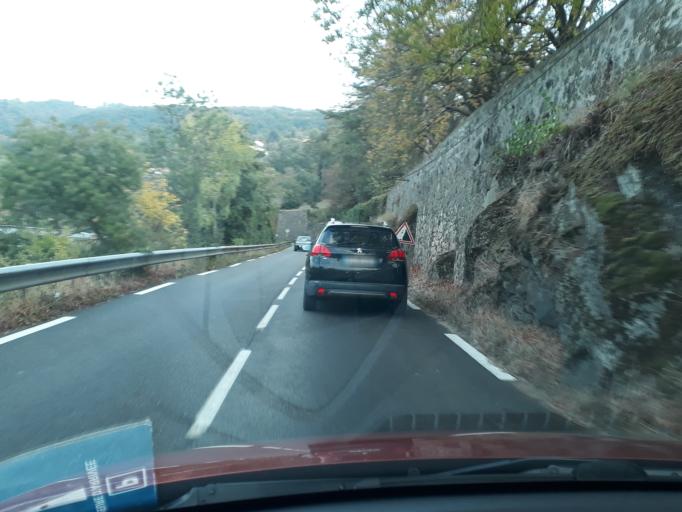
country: FR
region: Rhone-Alpes
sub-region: Departement de l'Isere
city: Les Roches-de-Condrieu
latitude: 45.4537
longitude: 4.7737
